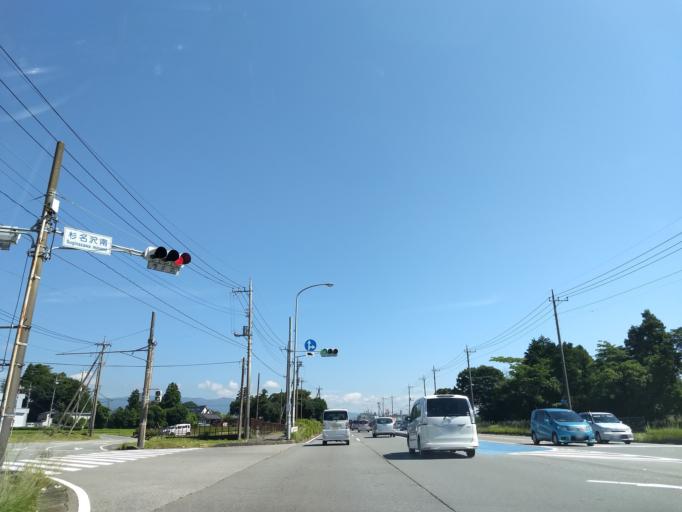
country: JP
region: Shizuoka
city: Gotemba
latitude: 35.2883
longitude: 138.9194
